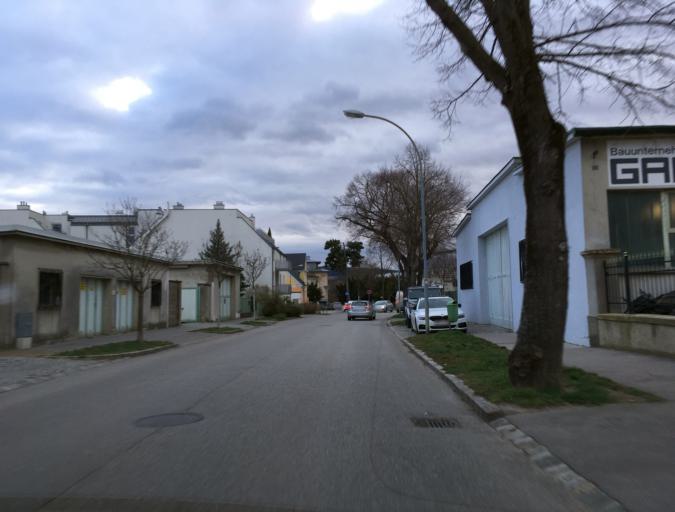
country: AT
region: Lower Austria
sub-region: Politischer Bezirk Korneuburg
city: Korneuburg
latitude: 48.3415
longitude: 16.3334
